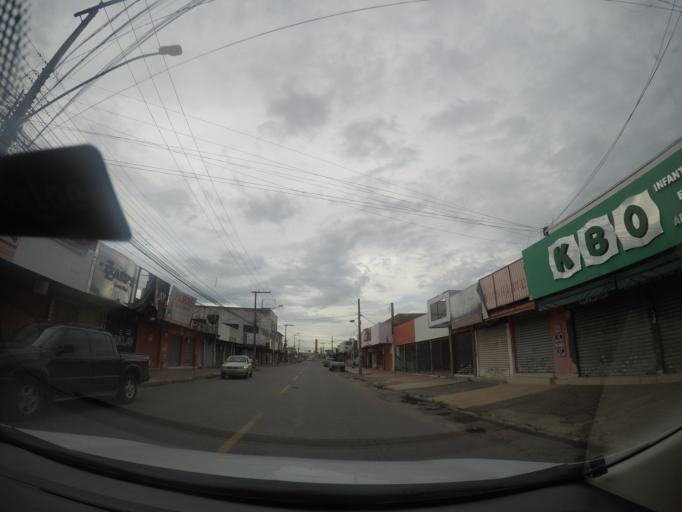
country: BR
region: Goias
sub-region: Goiania
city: Goiania
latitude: -16.6590
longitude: -49.2720
